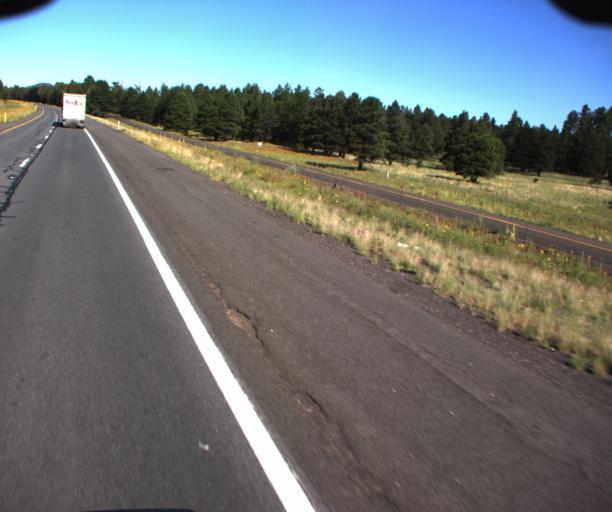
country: US
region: Arizona
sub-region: Coconino County
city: Parks
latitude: 35.2453
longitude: -111.8412
